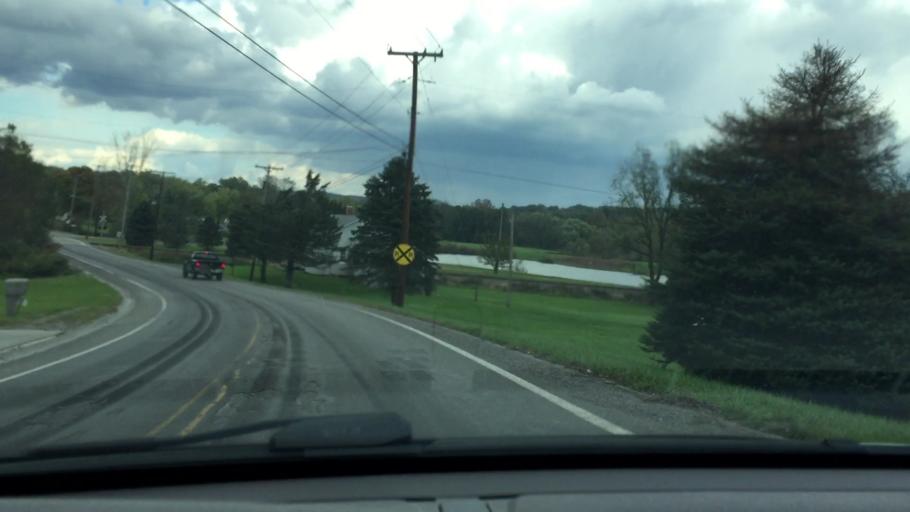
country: US
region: Pennsylvania
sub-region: Lawrence County
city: Oakwood
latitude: 41.0088
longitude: -80.4365
